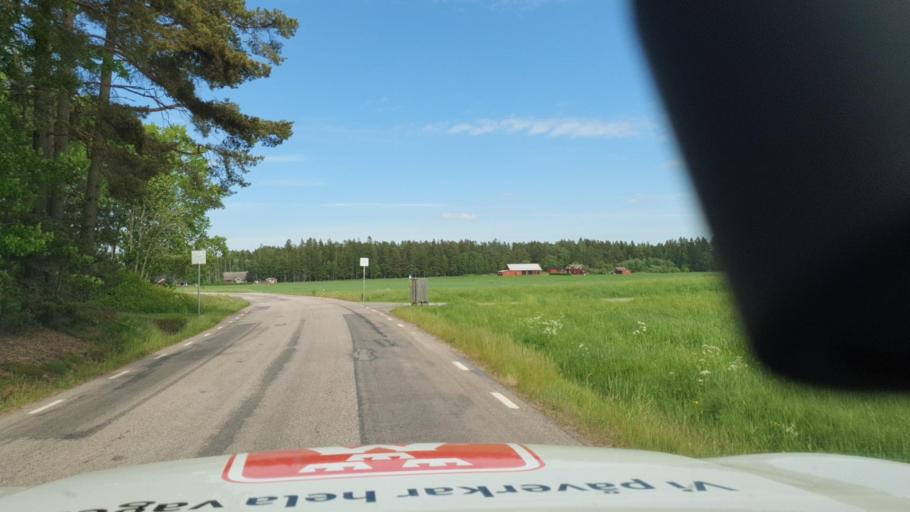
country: SE
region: Vaestra Goetaland
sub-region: Essunga Kommun
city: Nossebro
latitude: 58.2237
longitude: 12.6496
